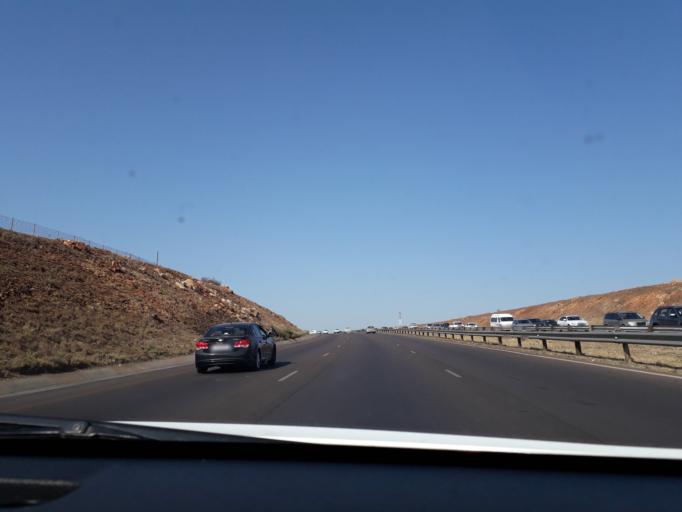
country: ZA
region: Gauteng
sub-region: City of Tshwane Metropolitan Municipality
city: Pretoria
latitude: -25.7918
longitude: 28.1848
